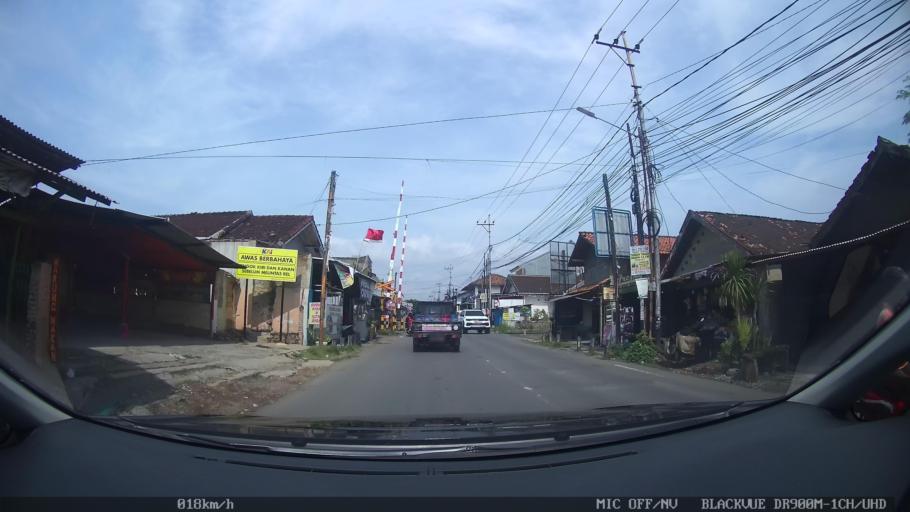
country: ID
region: Lampung
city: Kedaton
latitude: -5.3866
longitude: 105.2663
